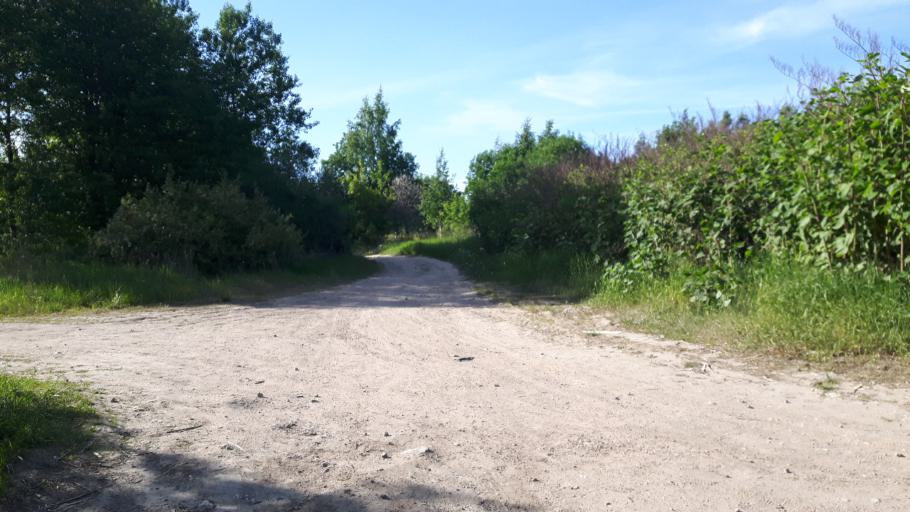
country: EE
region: Harju
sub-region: Tallinna linn
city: Kose
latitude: 59.4457
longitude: 24.9063
